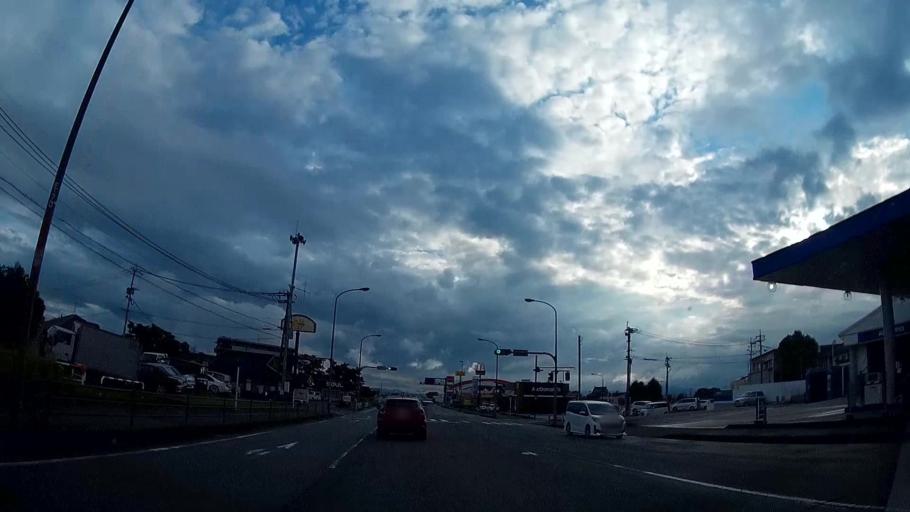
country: JP
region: Kumamoto
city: Ozu
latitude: 32.8787
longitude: 130.8870
